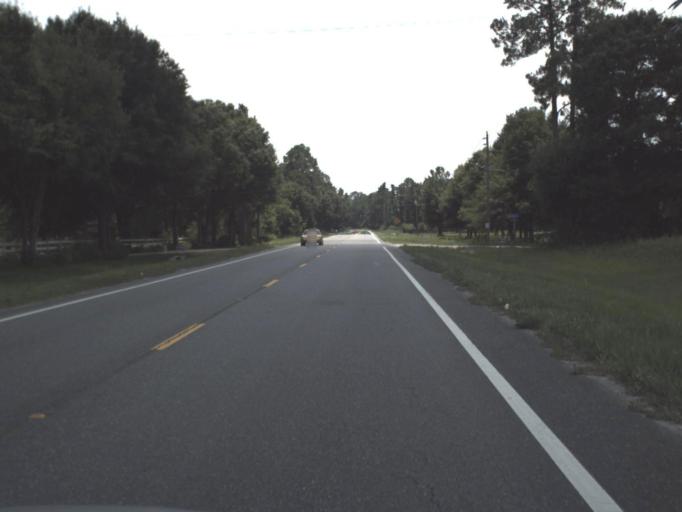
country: US
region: Florida
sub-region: Bradford County
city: Starke
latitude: 30.0303
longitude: -82.1592
